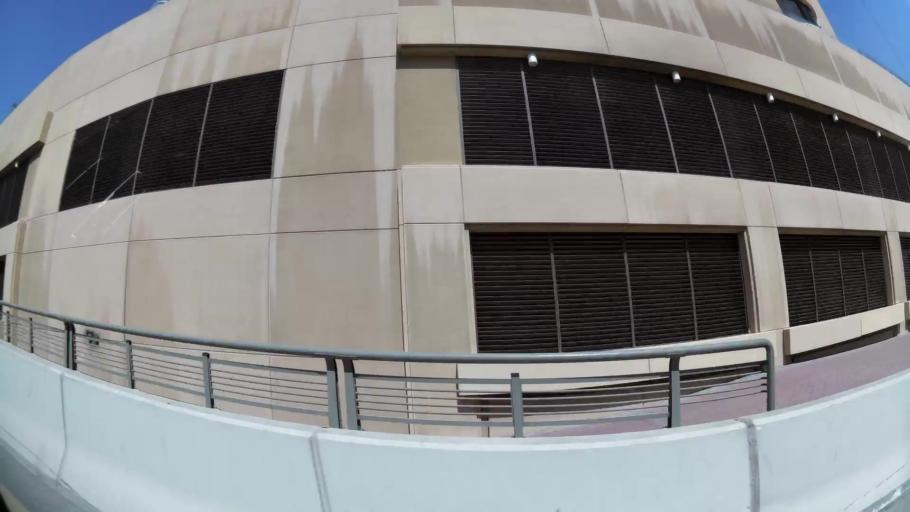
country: AE
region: Dubai
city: Dubai
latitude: 25.0864
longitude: 55.1430
